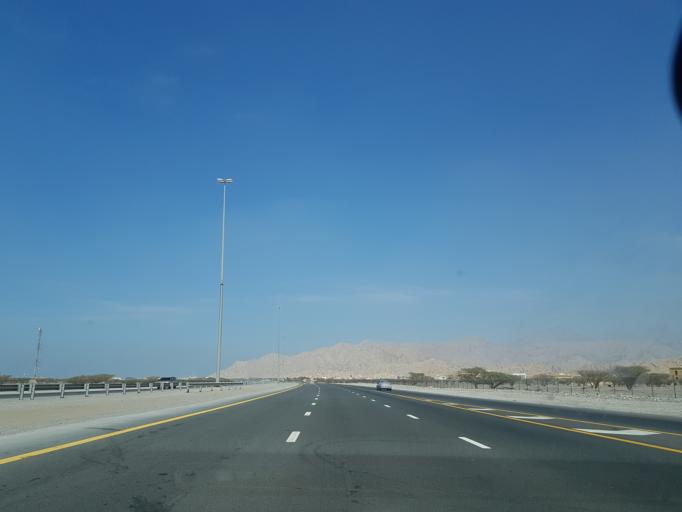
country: AE
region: Ra's al Khaymah
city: Ras al-Khaimah
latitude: 25.7828
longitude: 56.0312
